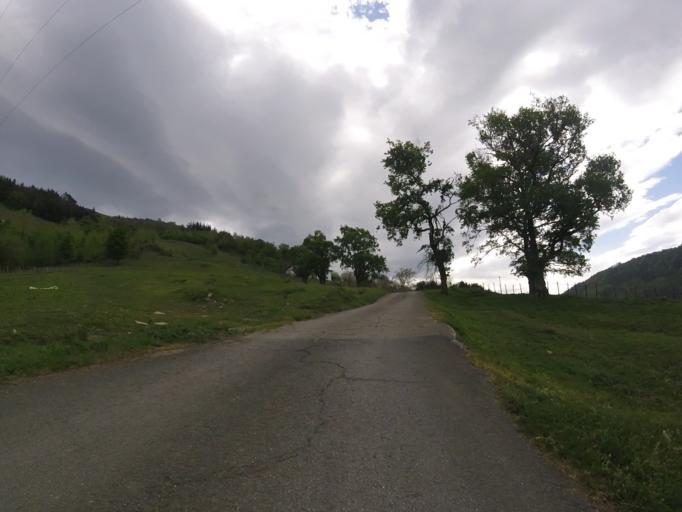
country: ES
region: Basque Country
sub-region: Provincia de Guipuzcoa
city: Aizarnazabal
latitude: 43.2550
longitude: -2.2266
